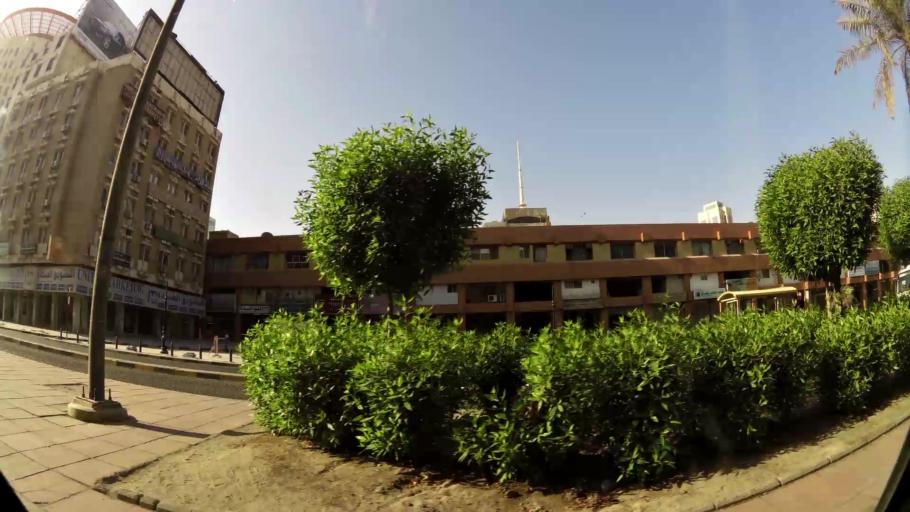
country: KW
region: Al Asimah
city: Kuwait City
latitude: 29.3732
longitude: 47.9808
